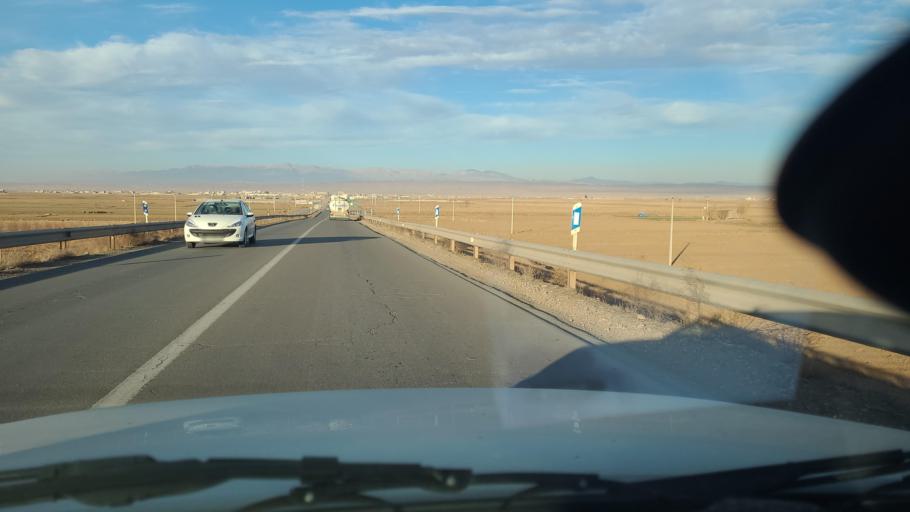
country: IR
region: Razavi Khorasan
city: Neqab
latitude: 36.6040
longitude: 57.5910
